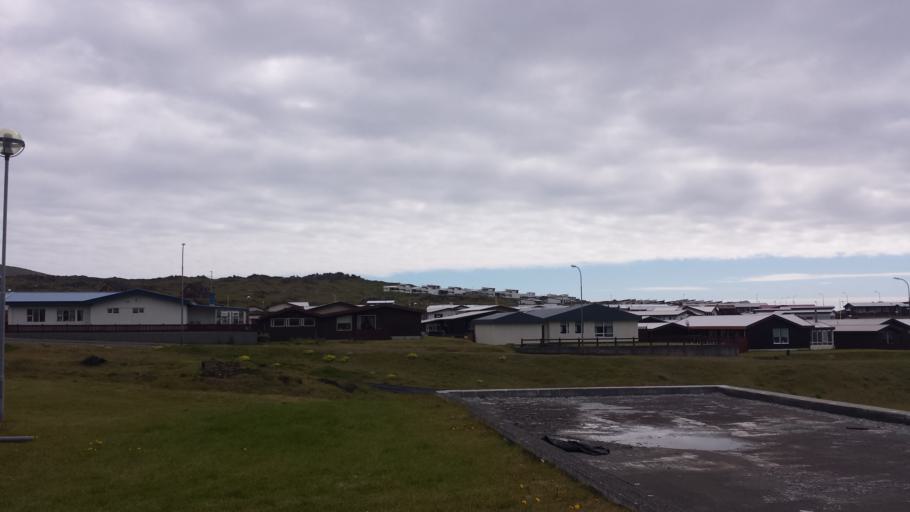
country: IS
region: South
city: Vestmannaeyjar
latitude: 63.4366
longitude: -20.2984
